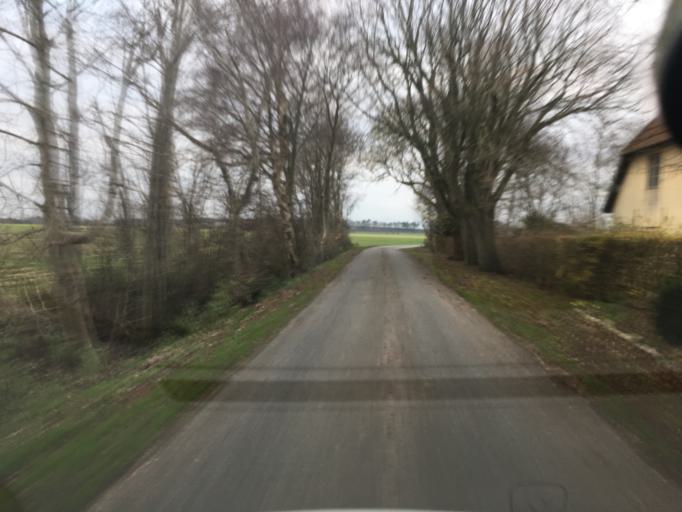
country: DK
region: South Denmark
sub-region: Tonder Kommune
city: Logumkloster
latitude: 55.0600
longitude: 9.0664
